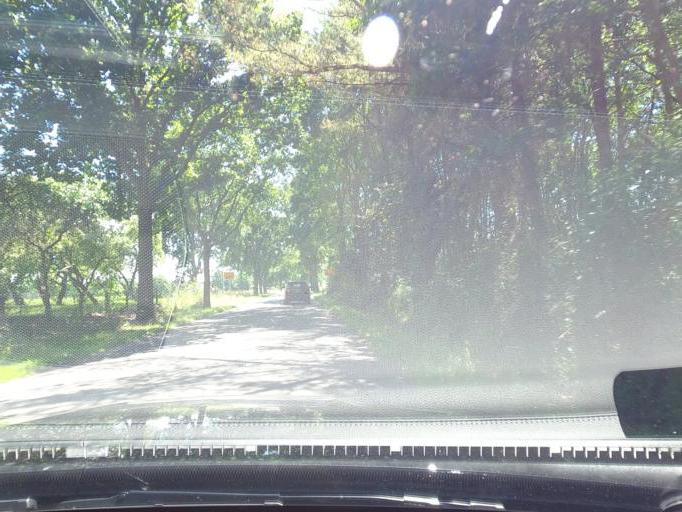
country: DE
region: Lower Saxony
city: Hohne
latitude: 52.5835
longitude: 10.3751
